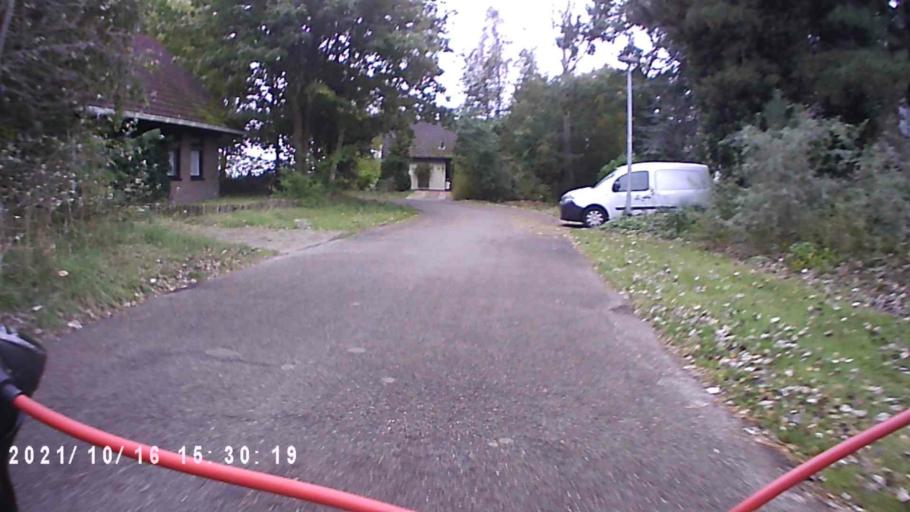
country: NL
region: Friesland
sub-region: Gemeente Dongeradeel
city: Anjum
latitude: 53.4042
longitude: 6.2210
